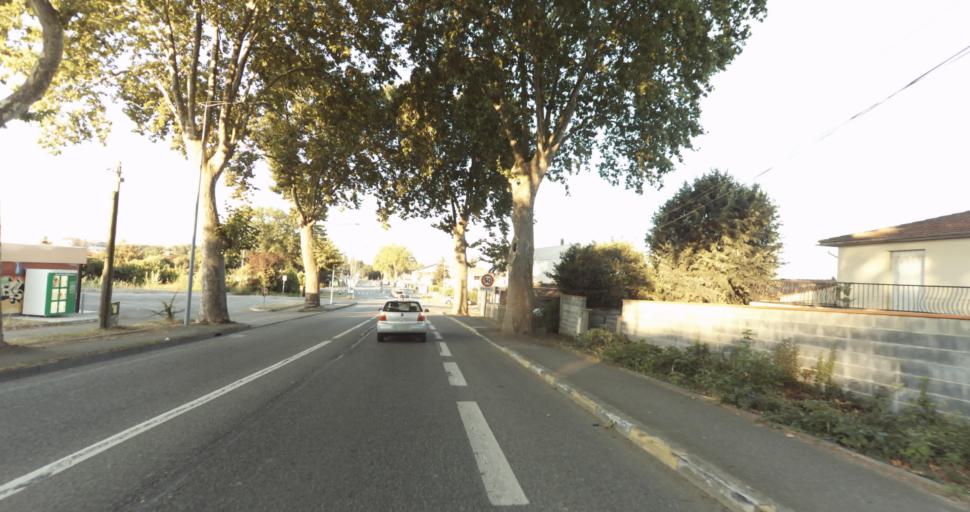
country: FR
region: Midi-Pyrenees
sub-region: Departement de la Haute-Garonne
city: L'Union
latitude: 43.6576
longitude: 1.4808
